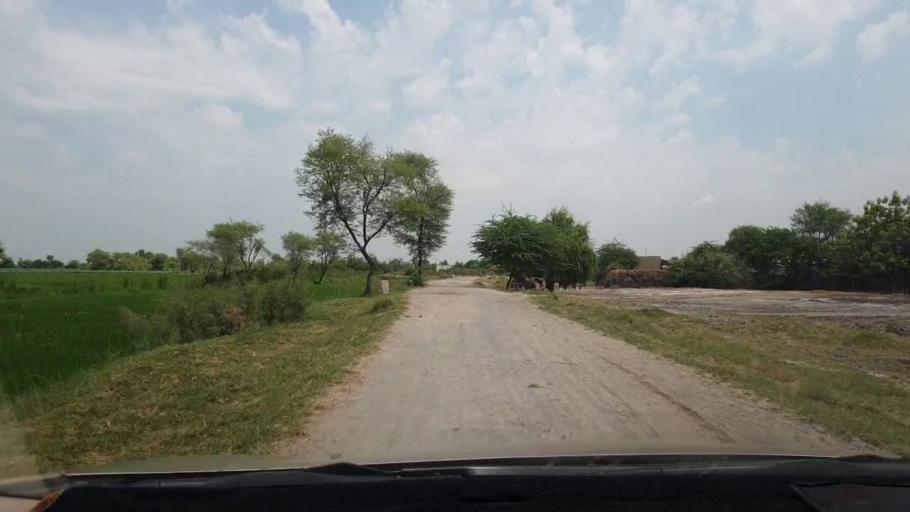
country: PK
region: Sindh
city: Naudero
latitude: 27.7283
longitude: 68.3504
